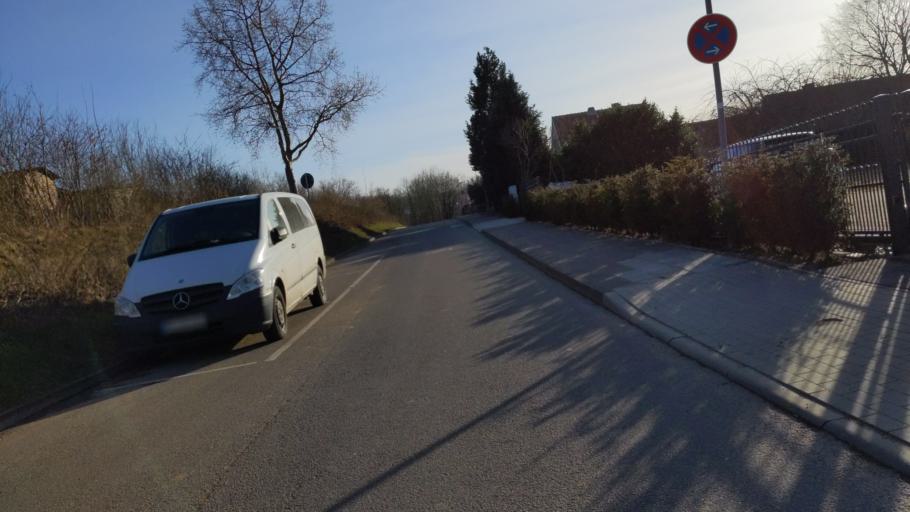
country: DE
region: Schleswig-Holstein
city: Scharbeutz
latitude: 54.0315
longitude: 10.7420
